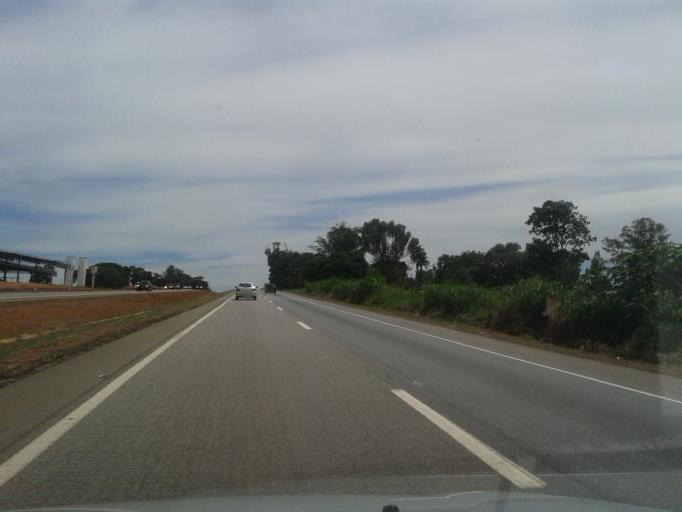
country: BR
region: Goias
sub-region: Hidrolandia
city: Hidrolandia
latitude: -17.0449
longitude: -49.2254
